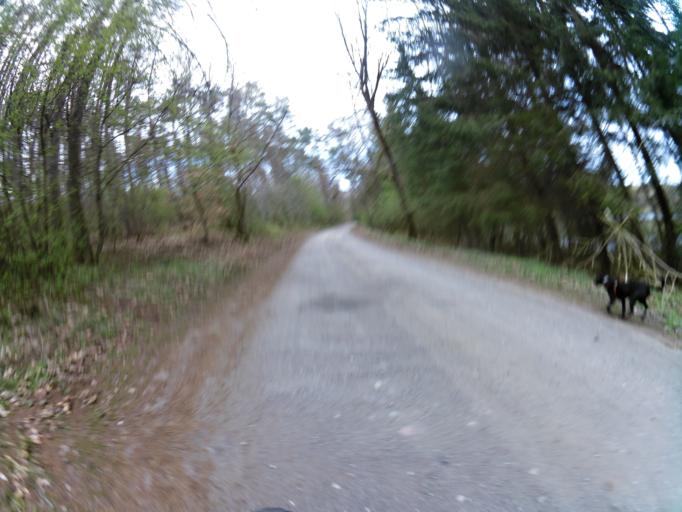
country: PL
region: West Pomeranian Voivodeship
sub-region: Powiat koszalinski
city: Bobolice
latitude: 53.8576
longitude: 16.6834
